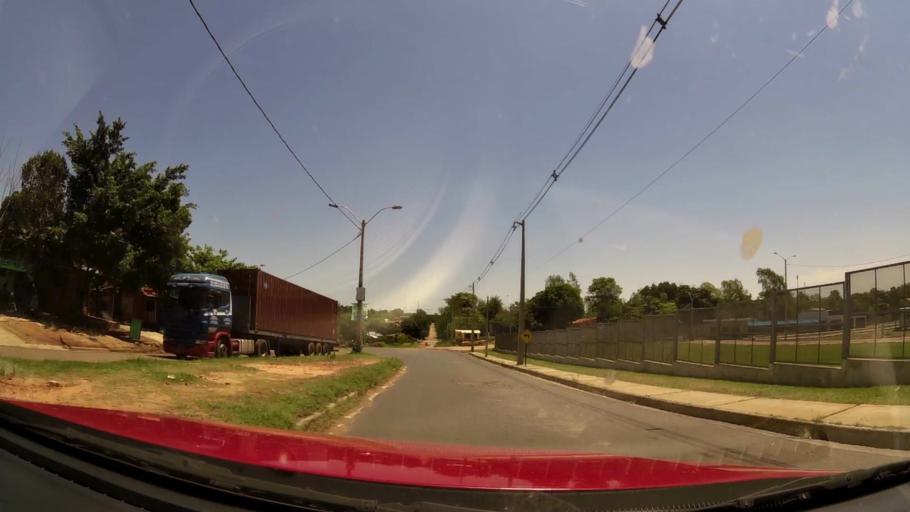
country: PY
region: Central
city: Colonia Mariano Roque Alonso
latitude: -25.2291
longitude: -57.5573
